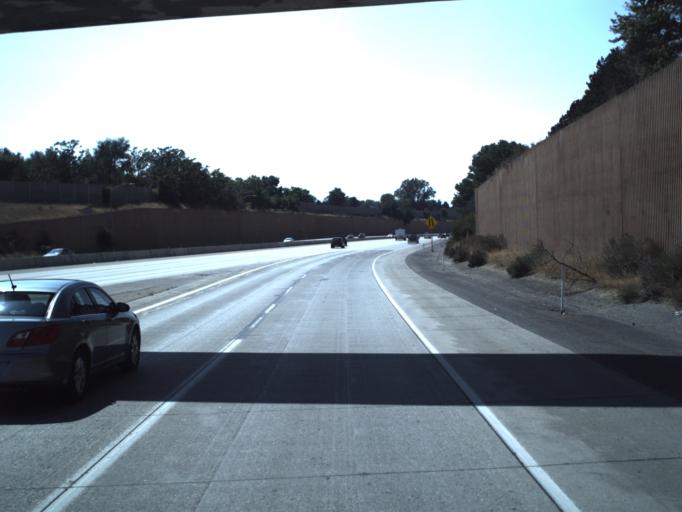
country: US
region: Utah
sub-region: Salt Lake County
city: Little Cottonwood Creek Valley
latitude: 40.6324
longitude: -111.8379
